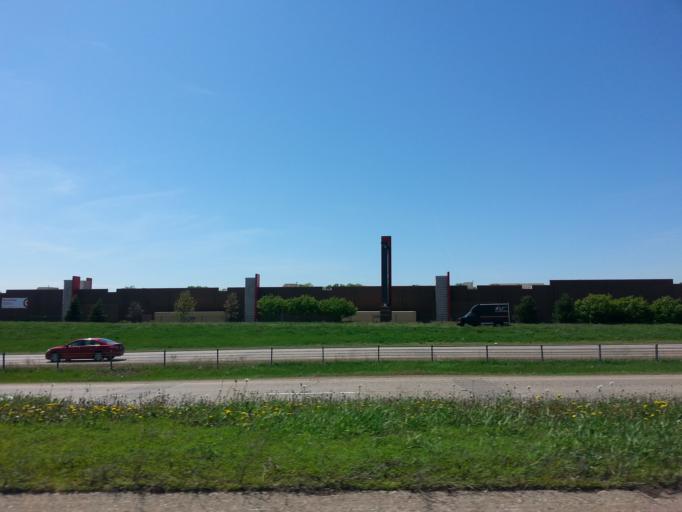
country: US
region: Minnesota
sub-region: Hennepin County
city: Richfield
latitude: 44.8857
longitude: -93.2465
